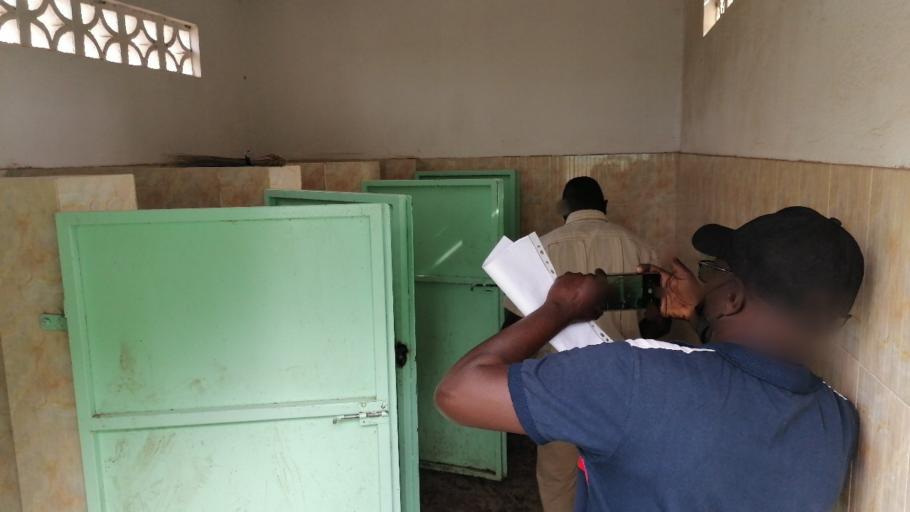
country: SN
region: Dakar
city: Pikine
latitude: 14.7707
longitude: -17.3790
